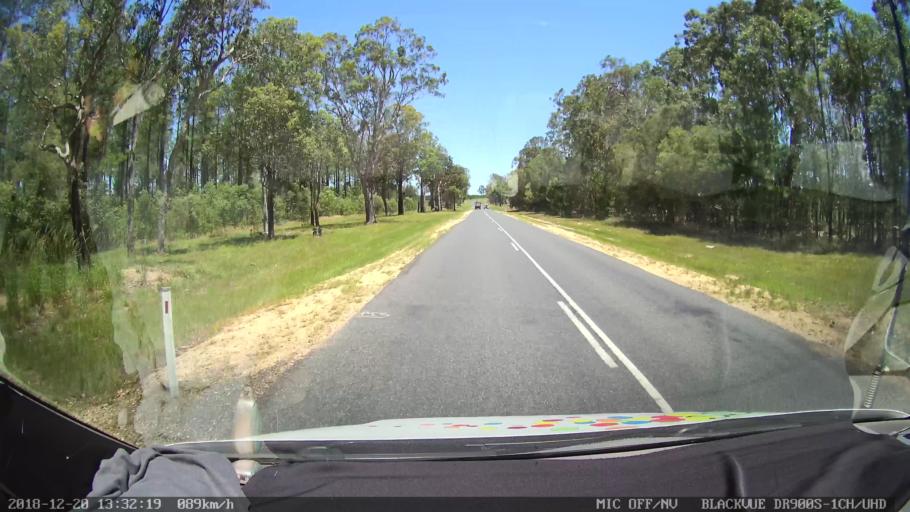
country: AU
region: New South Wales
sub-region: Clarence Valley
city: Gordon
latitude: -29.2303
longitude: 152.9890
